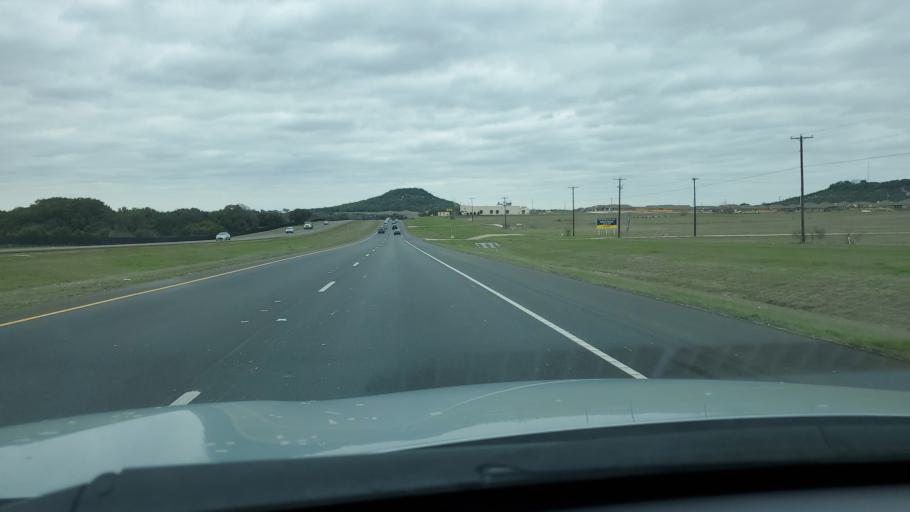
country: US
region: Texas
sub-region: Bell County
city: Killeen
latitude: 31.0296
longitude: -97.7571
